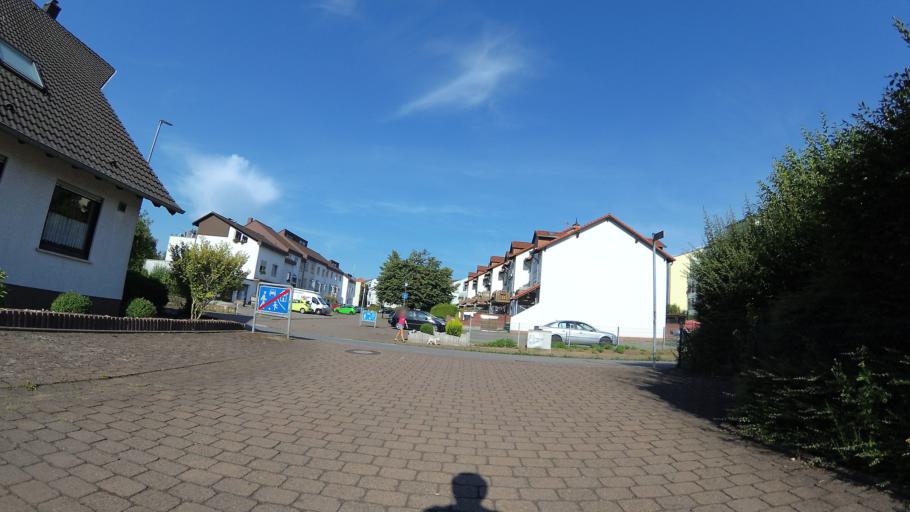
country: DE
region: Saarland
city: Homburg
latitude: 49.3406
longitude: 7.3224
